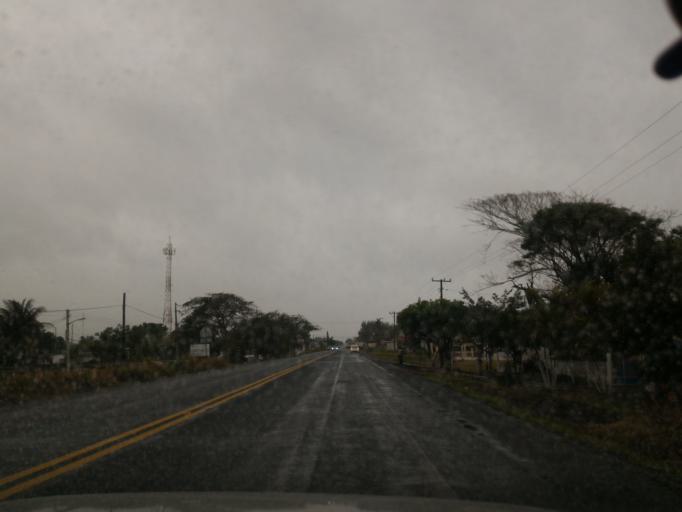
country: MX
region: Veracruz
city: Nautla
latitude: 20.2912
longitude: -96.8362
